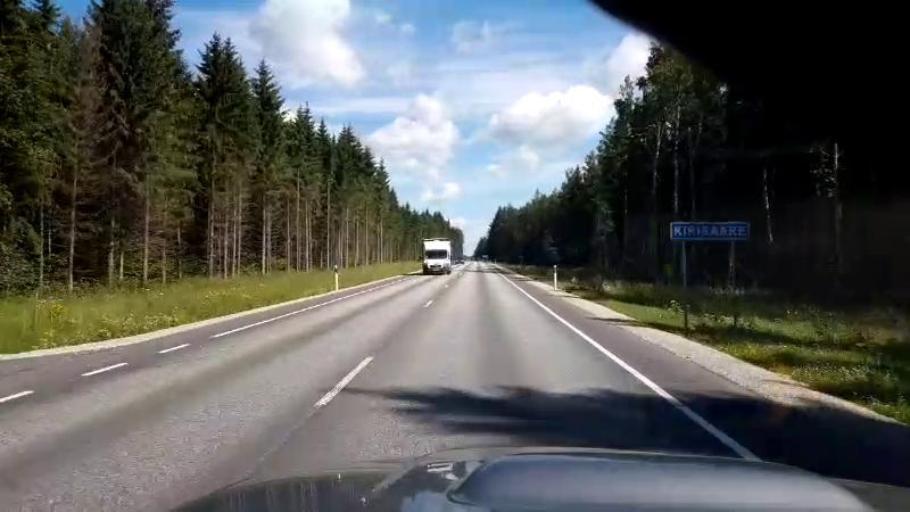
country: EE
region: Jaervamaa
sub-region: Paide linn
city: Paide
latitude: 58.9629
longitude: 25.6585
